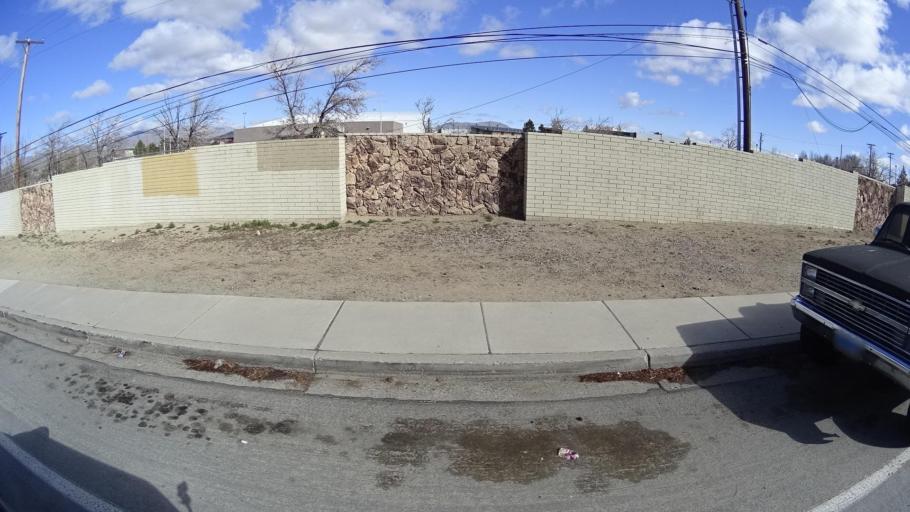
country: US
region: Nevada
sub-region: Washoe County
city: Lemmon Valley
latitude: 39.6541
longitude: -119.8791
